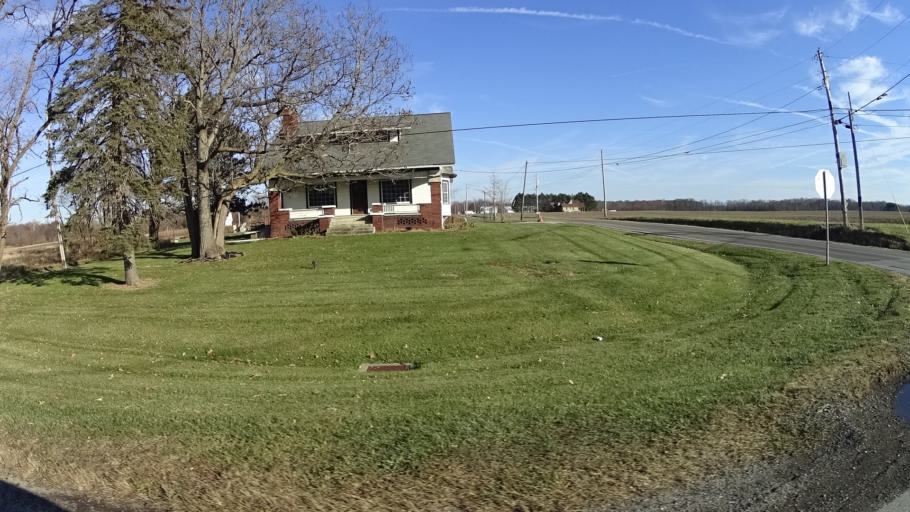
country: US
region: Ohio
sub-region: Lorain County
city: Wellington
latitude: 41.2000
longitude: -82.2166
